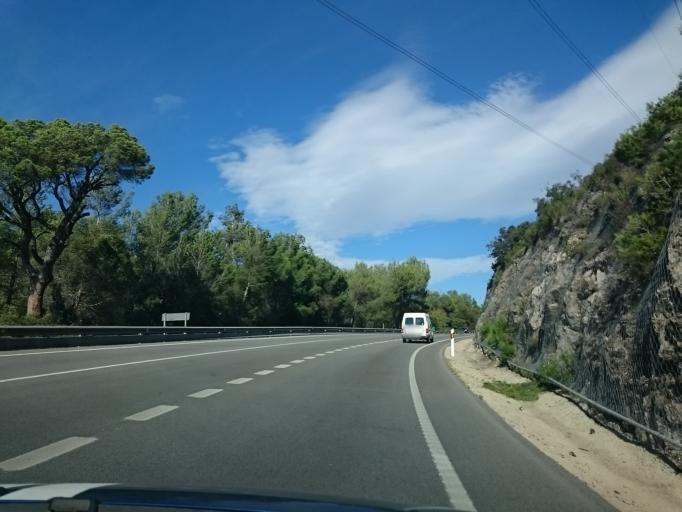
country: ES
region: Catalonia
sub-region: Provincia de Barcelona
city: Subirats
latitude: 41.3881
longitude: 1.8164
